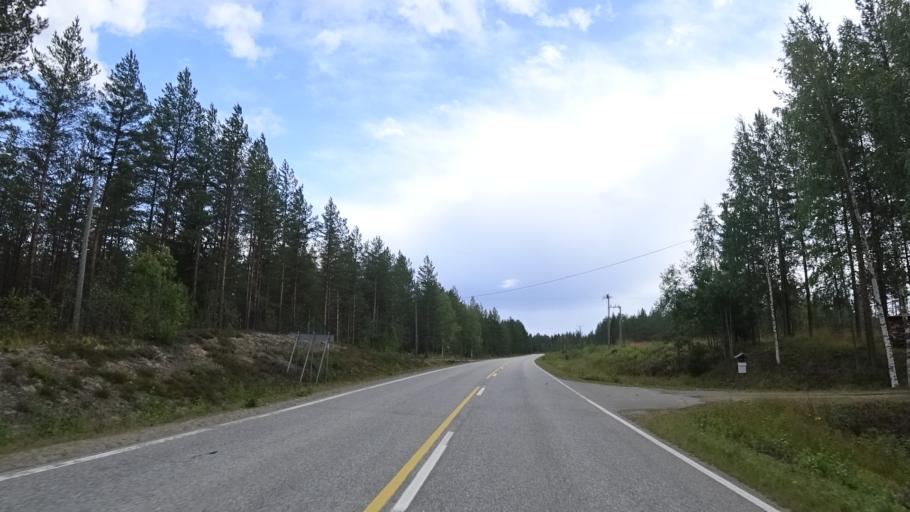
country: FI
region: North Karelia
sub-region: Joensuu
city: Ilomantsi
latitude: 62.6461
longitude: 31.0318
